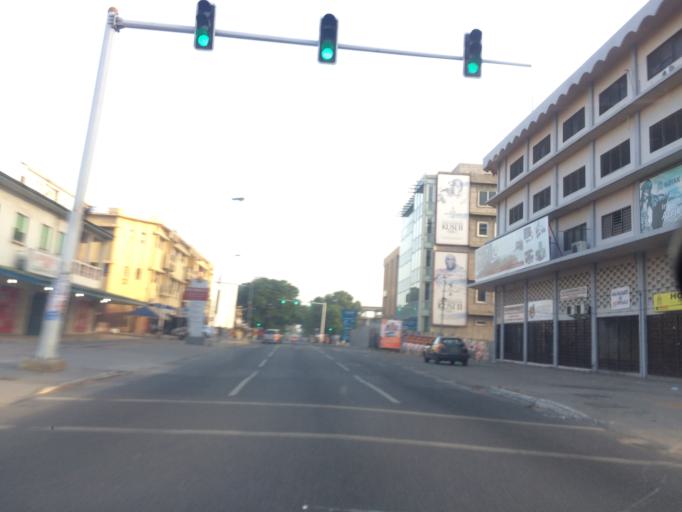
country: GH
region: Greater Accra
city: Accra
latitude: 5.5606
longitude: -0.2131
